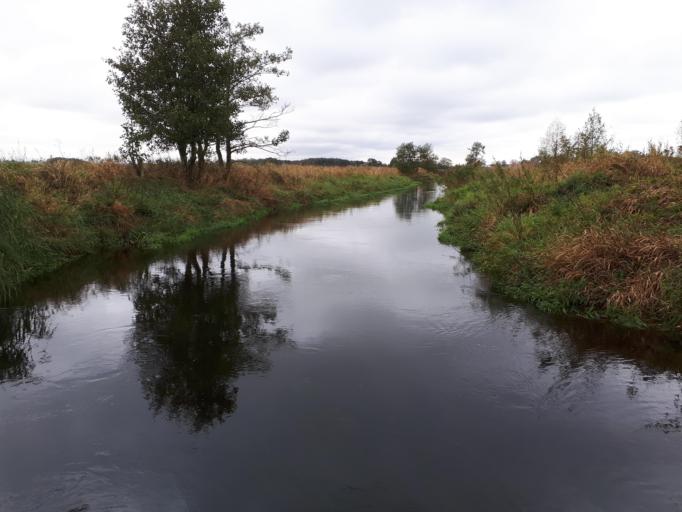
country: LT
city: Kalvarija
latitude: 54.4328
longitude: 23.3581
